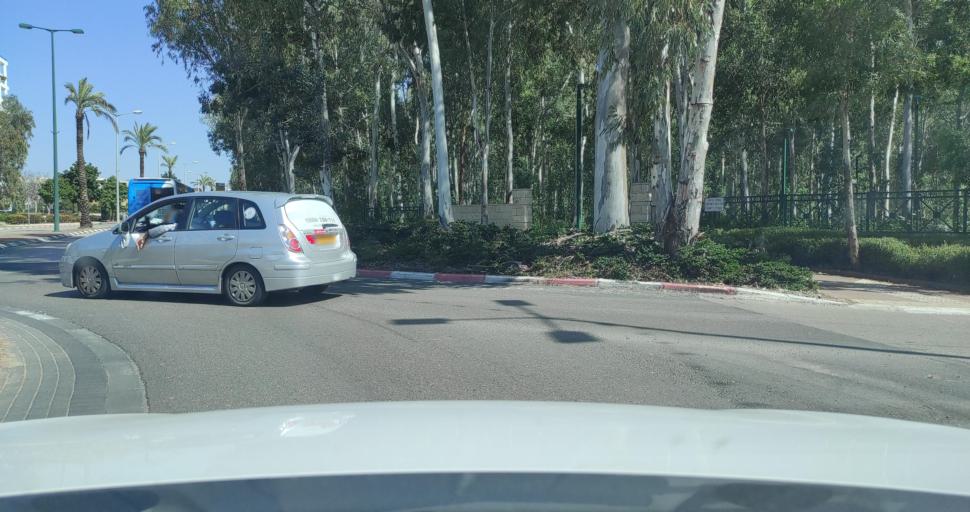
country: IL
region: Central District
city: Nordiyya
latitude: 32.3068
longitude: 34.8746
